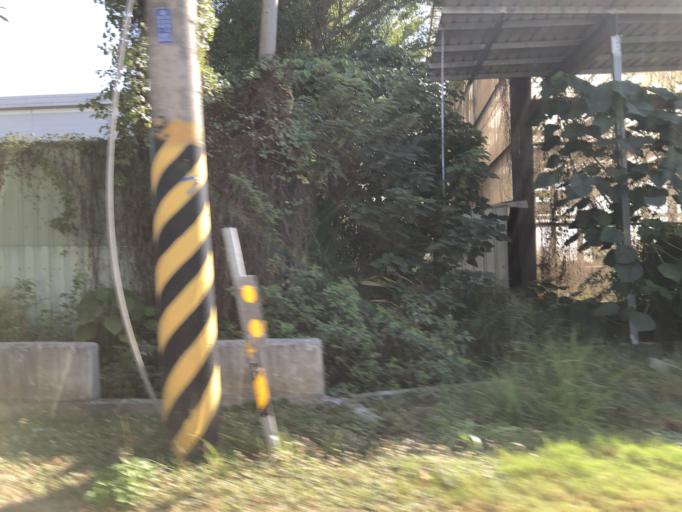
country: TW
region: Taiwan
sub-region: Tainan
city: Tainan
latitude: 23.0260
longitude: 120.2916
